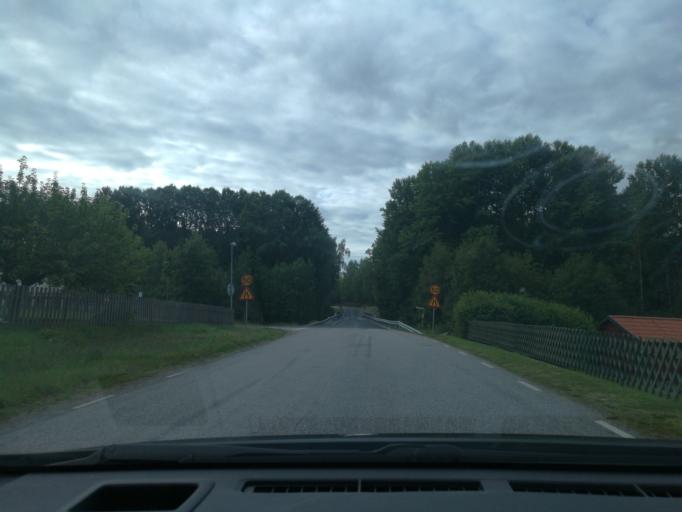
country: SE
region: Vaestmanland
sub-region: Kungsors Kommun
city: Kungsoer
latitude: 59.4063
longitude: 16.1075
